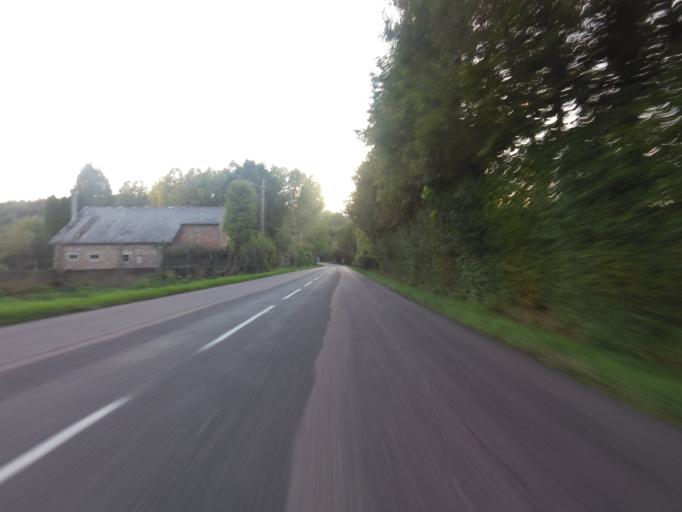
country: FR
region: Lower Normandy
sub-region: Departement de l'Orne
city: Vimoutiers
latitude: 48.9563
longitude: 0.2674
